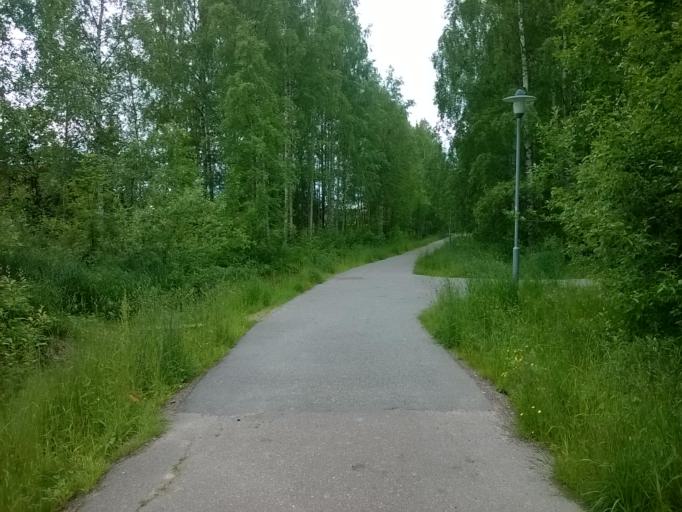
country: SE
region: Dalarna
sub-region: Saters Kommun
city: Saeter
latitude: 60.3397
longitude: 15.7493
